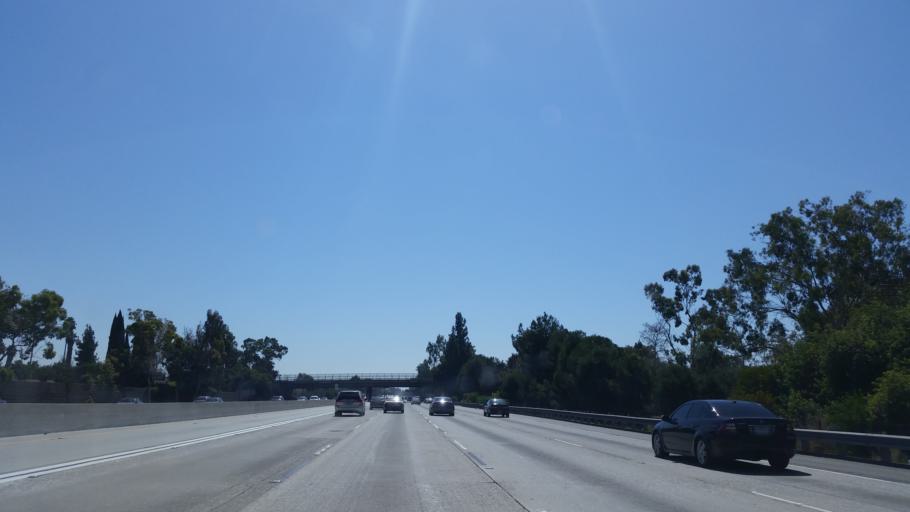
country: US
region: California
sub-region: Los Angeles County
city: Hawaiian Gardens
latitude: 33.8204
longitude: -118.0815
